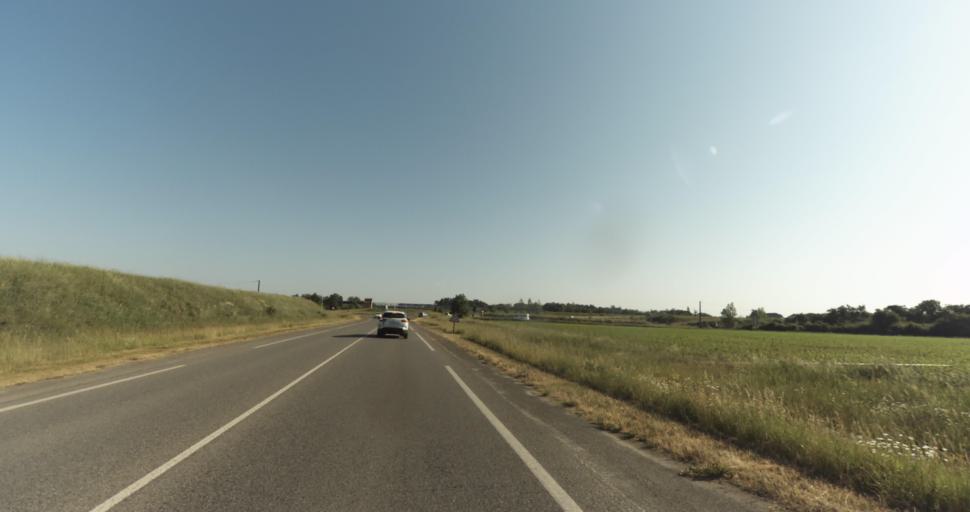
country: FR
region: Midi-Pyrenees
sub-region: Departement de la Haute-Garonne
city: Leguevin
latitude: 43.5791
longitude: 1.2175
